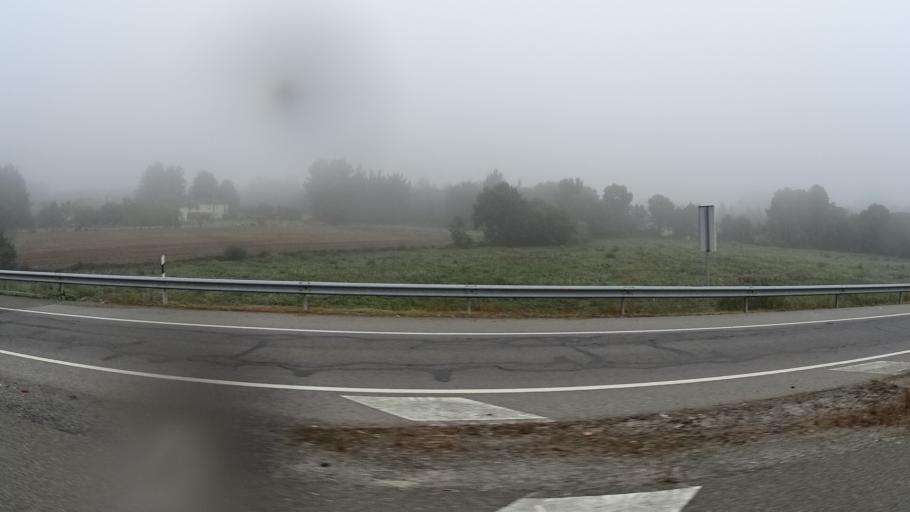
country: ES
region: Galicia
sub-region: Provincia de Lugo
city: Rabade
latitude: 43.1298
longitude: -7.6265
